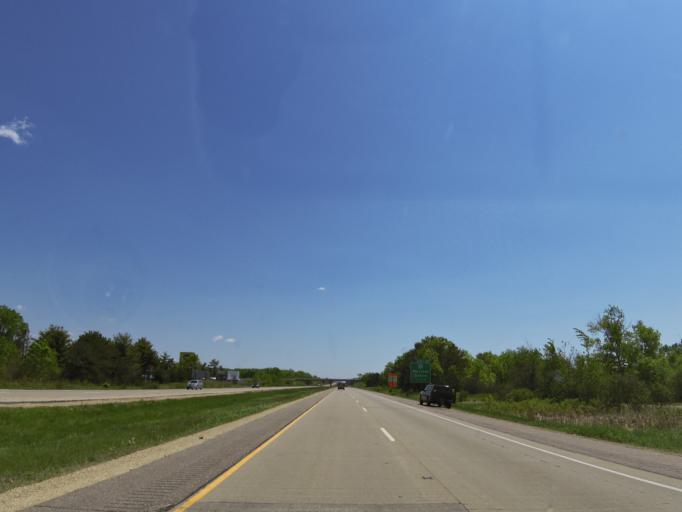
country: US
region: Wisconsin
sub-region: Juneau County
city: Mauston
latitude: 43.8156
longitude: -90.0761
